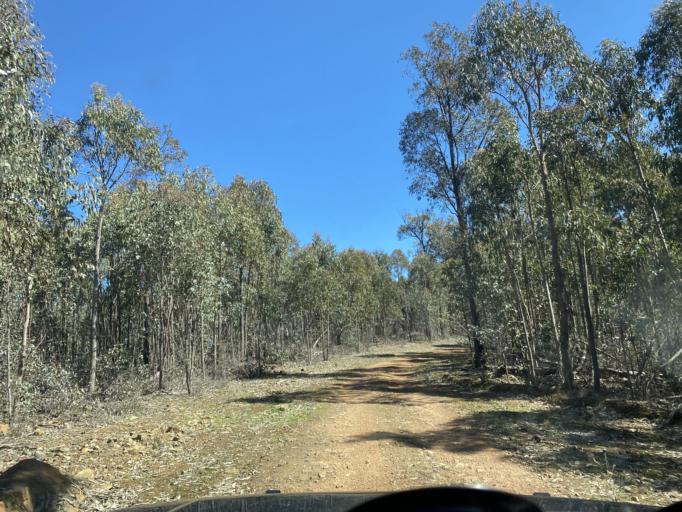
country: AU
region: Victoria
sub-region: Benalla
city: Benalla
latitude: -36.7254
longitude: 146.1813
